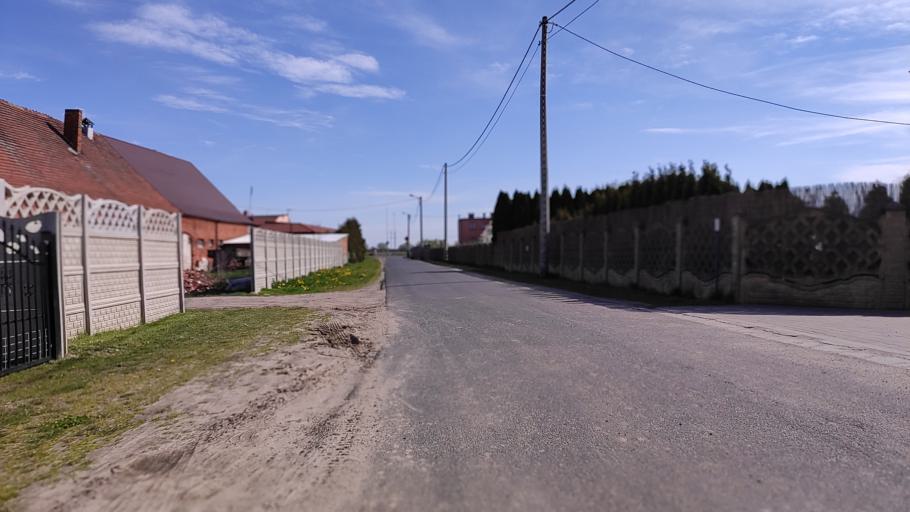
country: PL
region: Greater Poland Voivodeship
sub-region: Powiat poznanski
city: Kostrzyn
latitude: 52.3974
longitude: 17.1779
